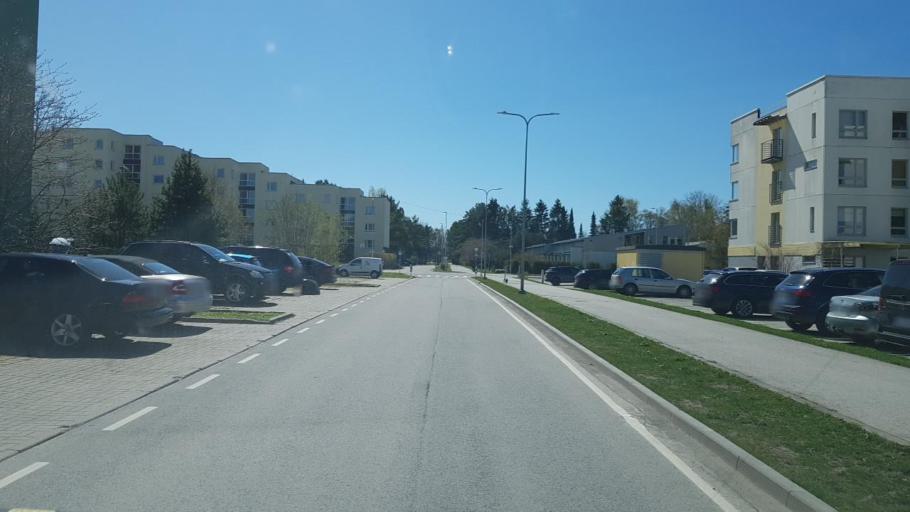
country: EE
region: Harju
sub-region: Viimsi vald
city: Haabneeme
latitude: 59.5136
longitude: 24.8271
